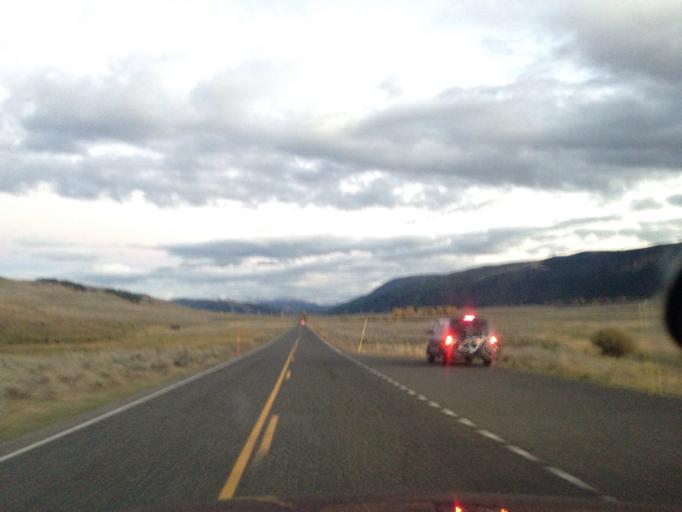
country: US
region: Montana
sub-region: Park County
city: Livingston
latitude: 44.8849
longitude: -110.2210
